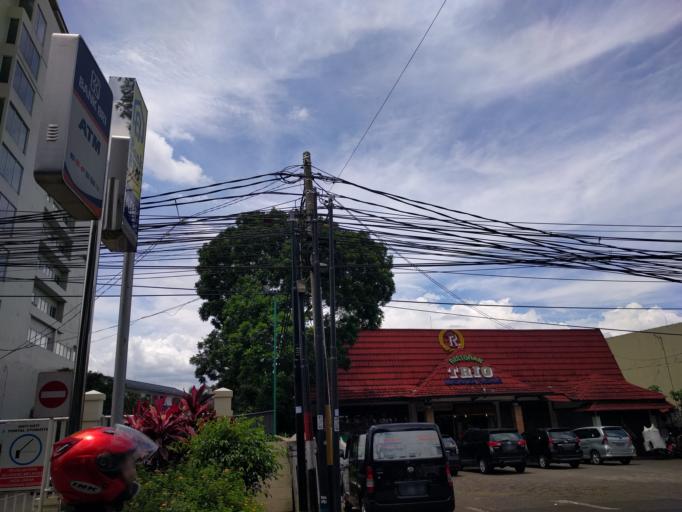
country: ID
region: West Java
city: Bogor
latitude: -6.5787
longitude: 106.8073
